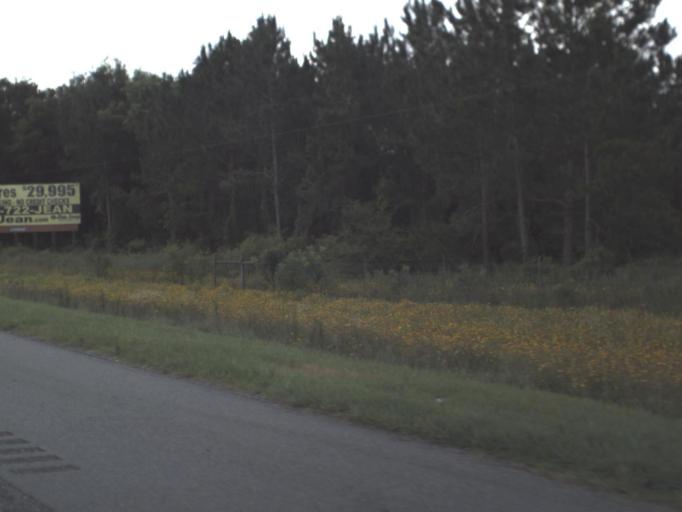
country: US
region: Florida
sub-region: Suwannee County
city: Wellborn
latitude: 30.2974
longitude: -82.7850
